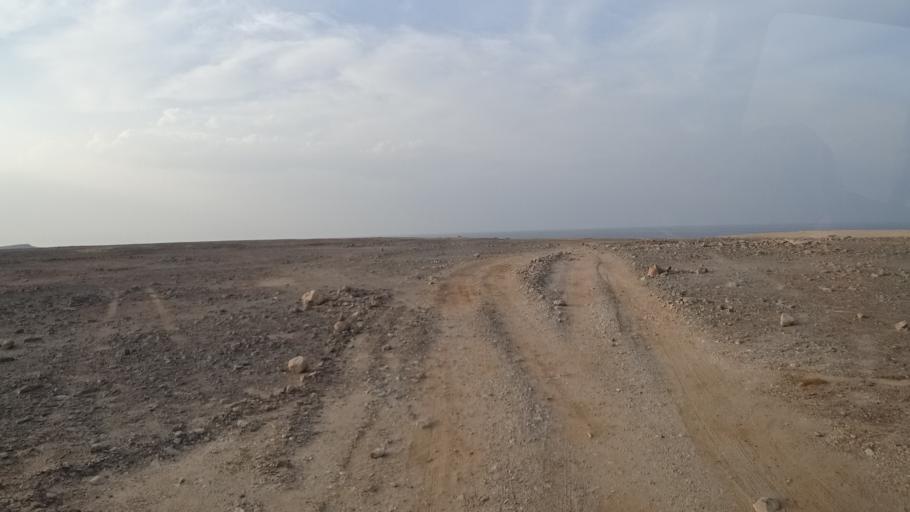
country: OM
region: Ash Sharqiyah
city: Sur
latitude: 22.4559
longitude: 59.8255
